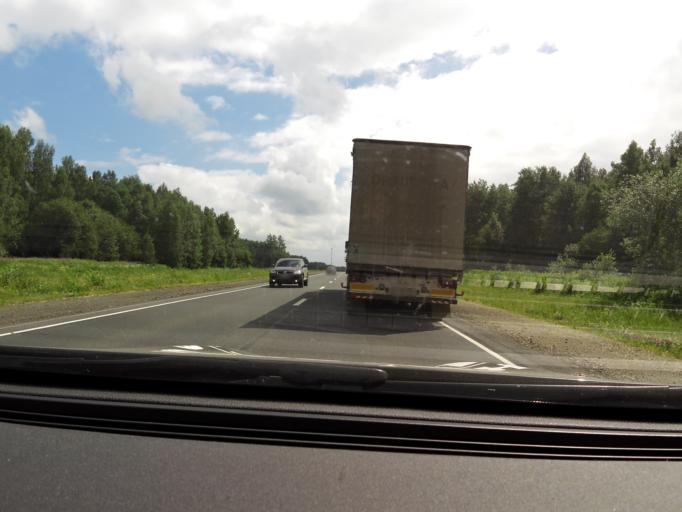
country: RU
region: Perm
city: Orda
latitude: 57.2058
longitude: 57.1009
